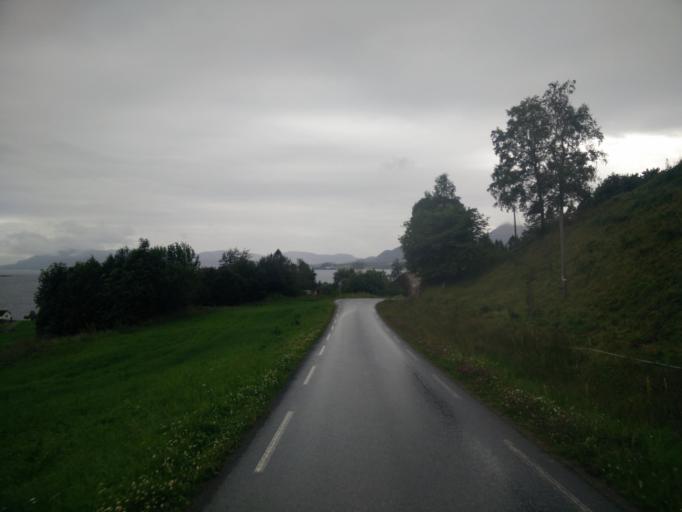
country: NO
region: More og Romsdal
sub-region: Kristiansund
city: Rensvik
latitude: 63.0164
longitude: 7.9074
